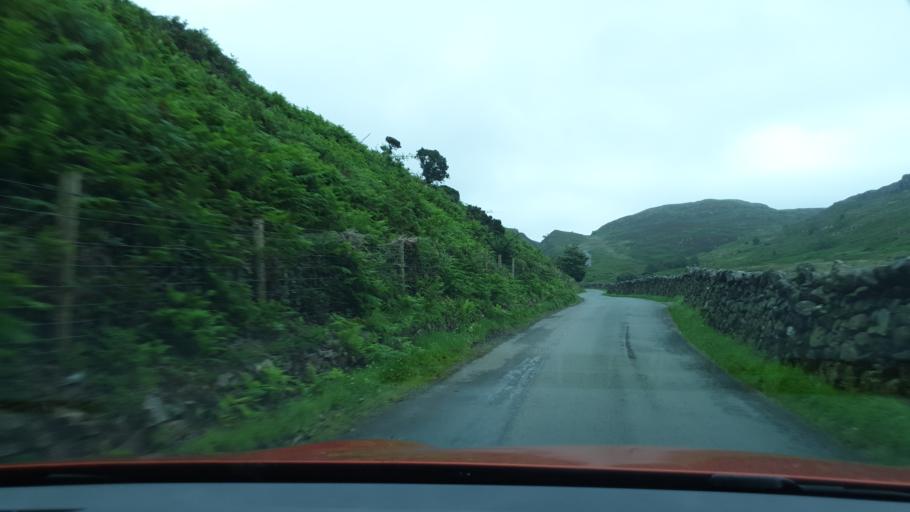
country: GB
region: England
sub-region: Cumbria
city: Millom
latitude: 54.3797
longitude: -3.3042
